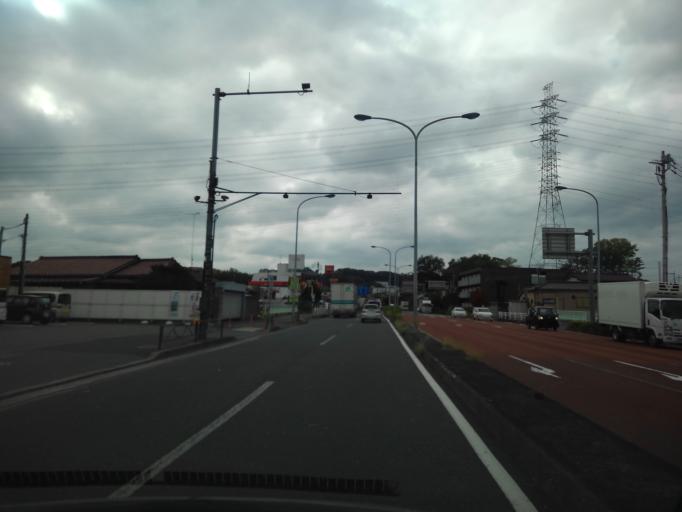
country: JP
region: Tokyo
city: Hachioji
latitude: 35.6839
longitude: 139.3456
